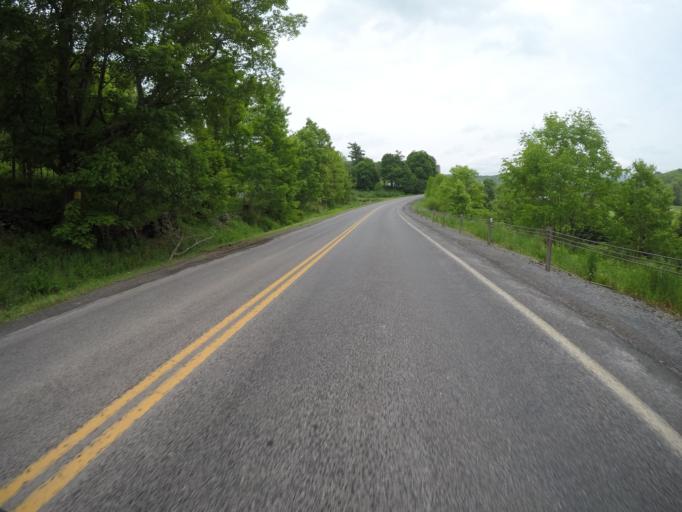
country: US
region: New York
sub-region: Delaware County
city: Delhi
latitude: 42.2696
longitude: -74.7462
